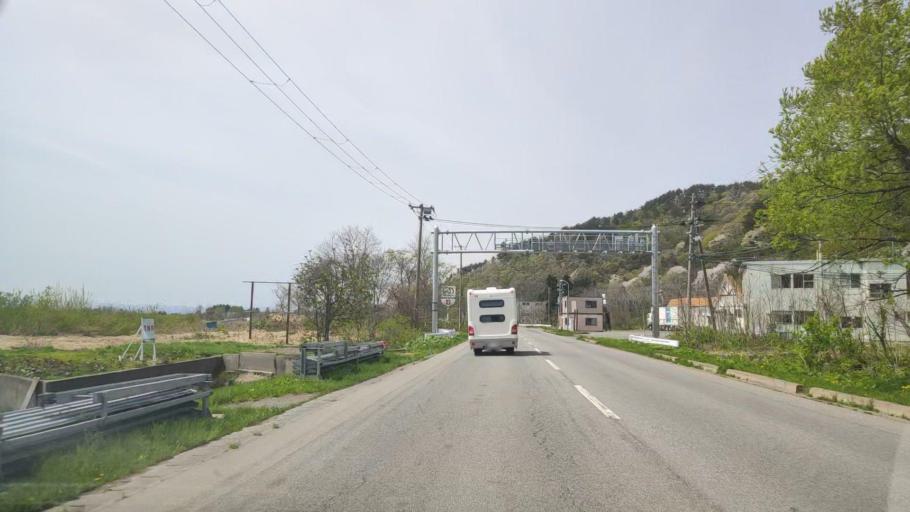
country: JP
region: Aomori
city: Aomori Shi
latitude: 40.8285
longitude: 140.8520
